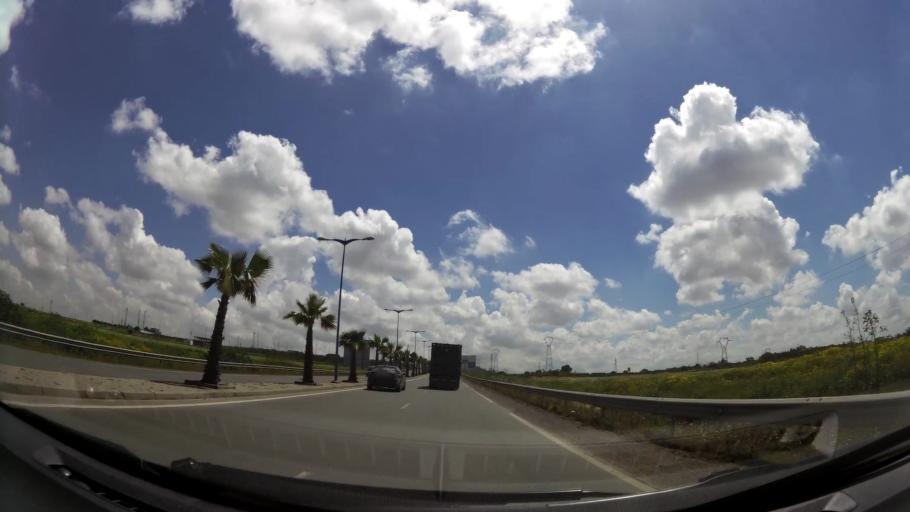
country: MA
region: Grand Casablanca
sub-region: Casablanca
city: Casablanca
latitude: 33.5155
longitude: -7.6143
